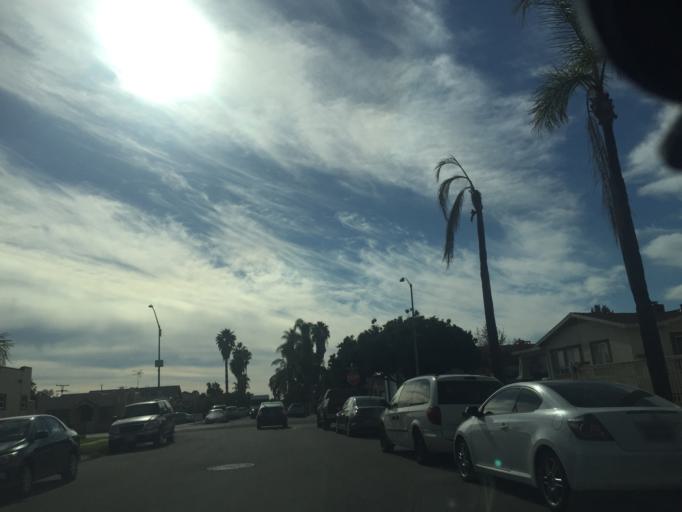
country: US
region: California
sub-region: San Diego County
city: Lemon Grove
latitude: 32.7536
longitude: -117.0955
